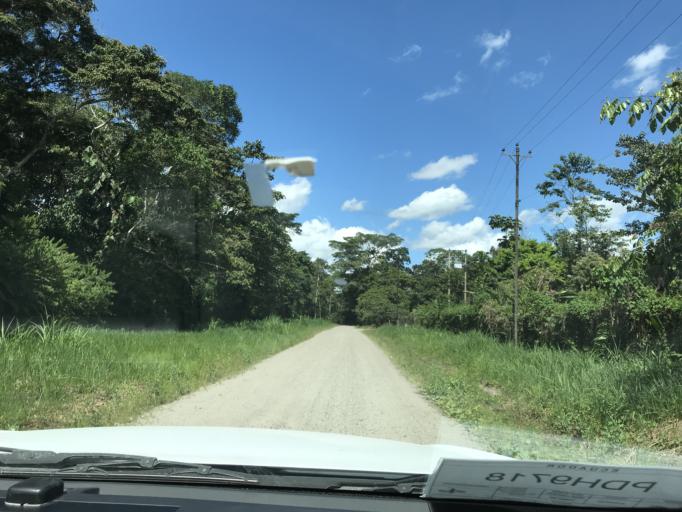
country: EC
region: Orellana
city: Puerto Francisco de Orellana
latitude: -0.4469
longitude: -76.6073
